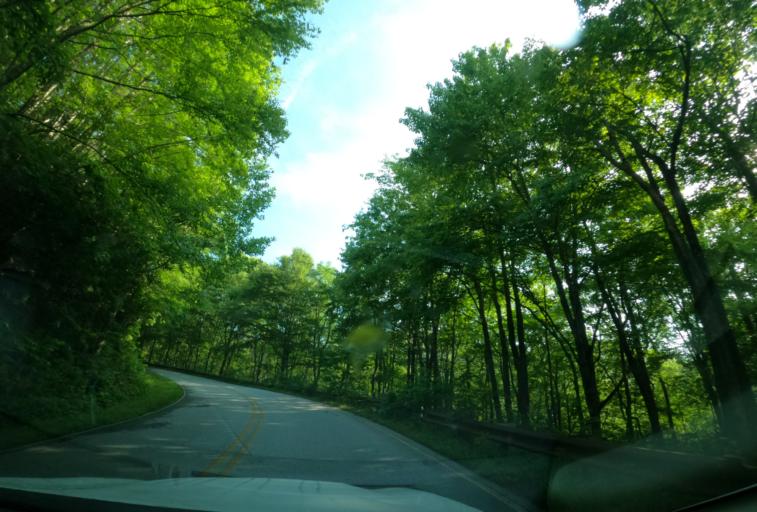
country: US
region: North Carolina
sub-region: Transylvania County
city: Brevard
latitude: 35.2579
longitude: -82.9086
